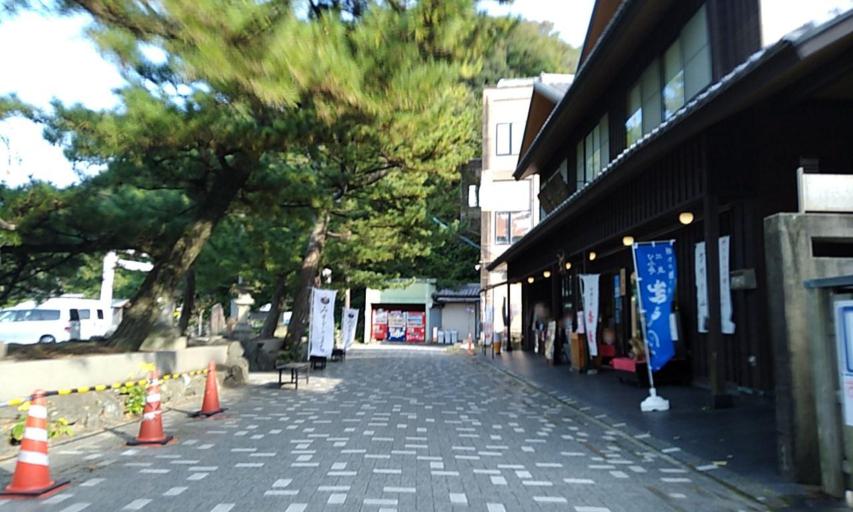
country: JP
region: Mie
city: Toba
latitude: 34.5084
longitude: 136.7862
